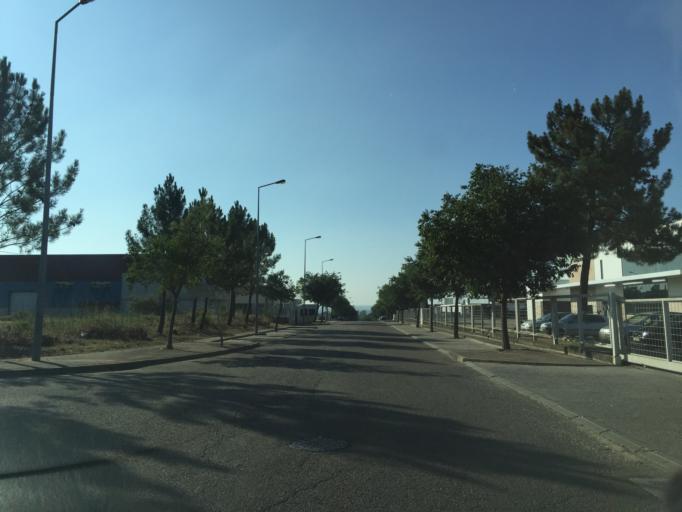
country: PT
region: Santarem
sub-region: Abrantes
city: Alferrarede
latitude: 39.4919
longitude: -8.1864
